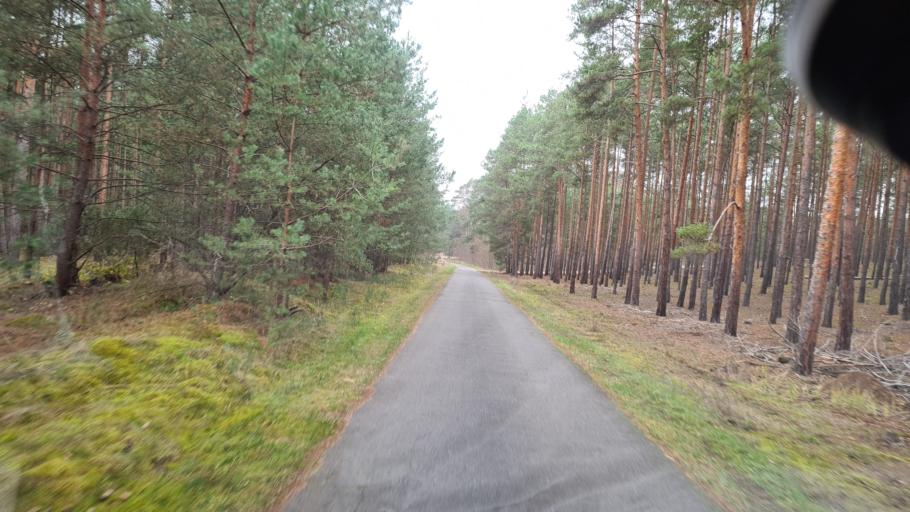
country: DE
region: Brandenburg
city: Schenkendobern
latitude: 51.9746
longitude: 14.6384
